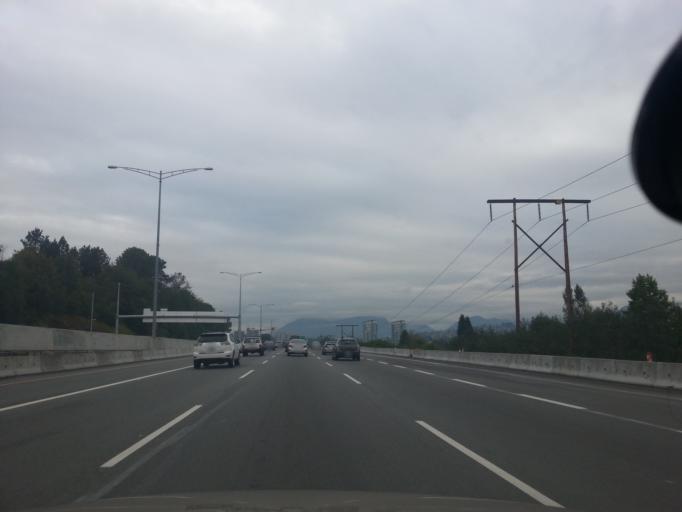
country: CA
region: British Columbia
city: Burnaby
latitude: 49.2522
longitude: -122.9752
